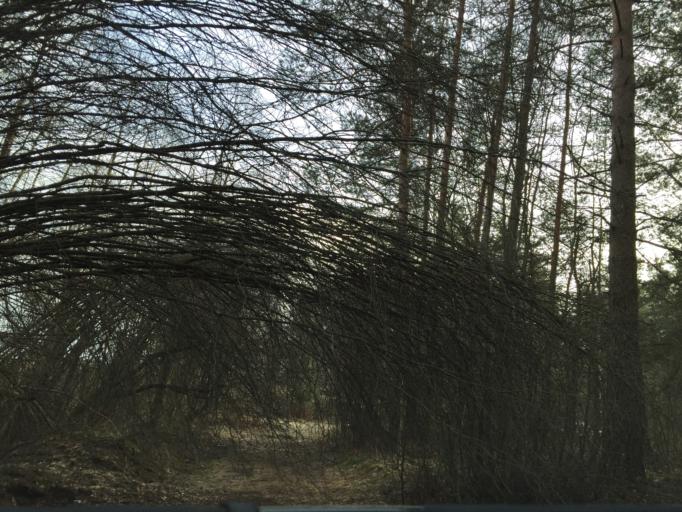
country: LV
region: Stopini
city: Ulbroka
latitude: 56.9214
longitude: 24.3063
